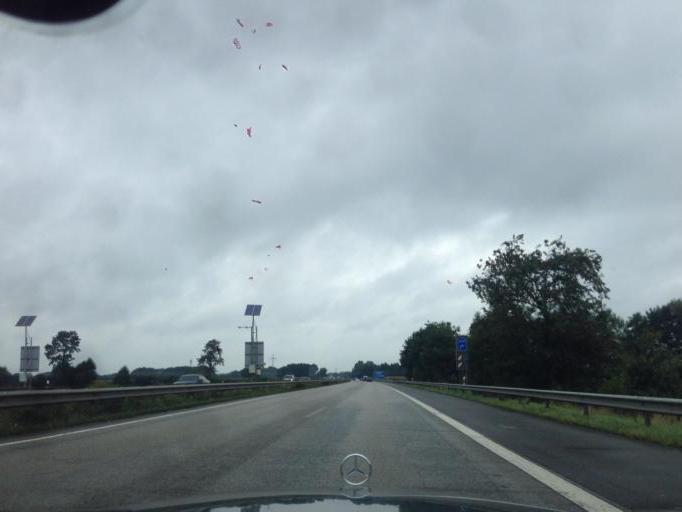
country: DE
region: Schleswig-Holstein
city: Padenstedt
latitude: 54.0324
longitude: 9.9324
